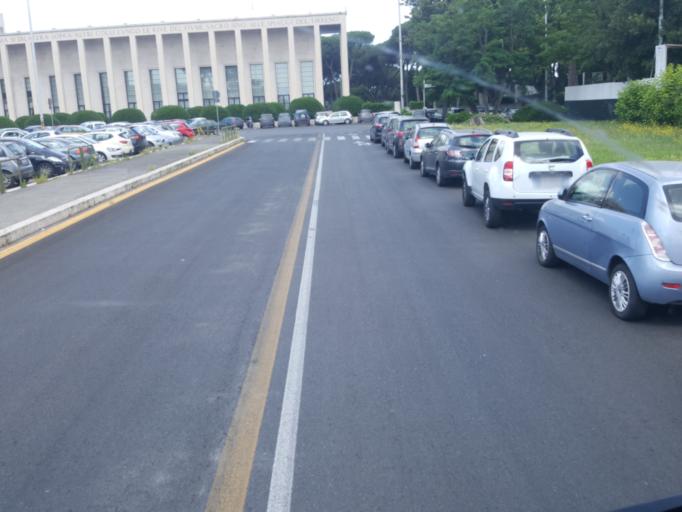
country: VA
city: Vatican City
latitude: 41.8373
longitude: 12.4708
